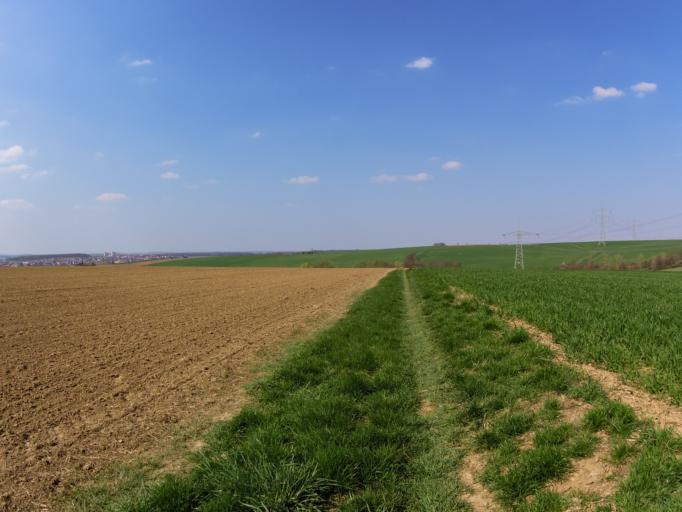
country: DE
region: Bavaria
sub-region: Regierungsbezirk Unterfranken
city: Rottendorf
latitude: 49.7799
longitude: 10.0465
